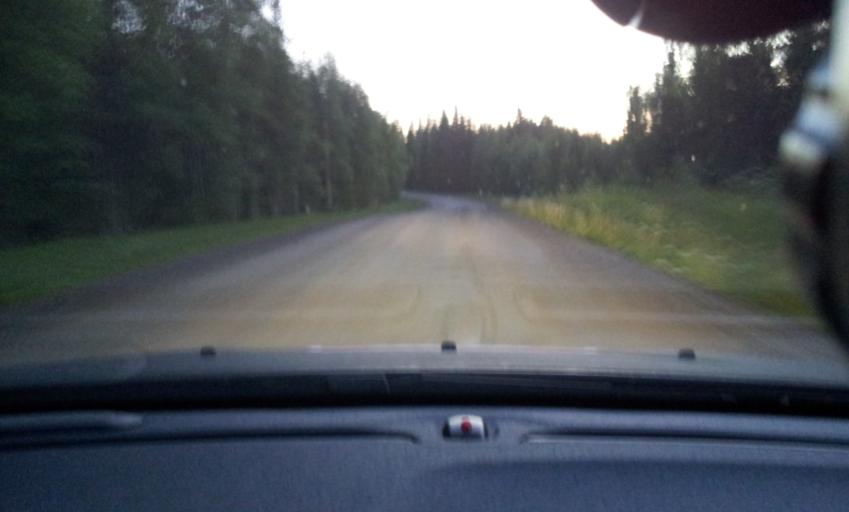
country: SE
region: Jaemtland
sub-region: Braecke Kommun
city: Braecke
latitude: 62.7371
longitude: 15.4572
